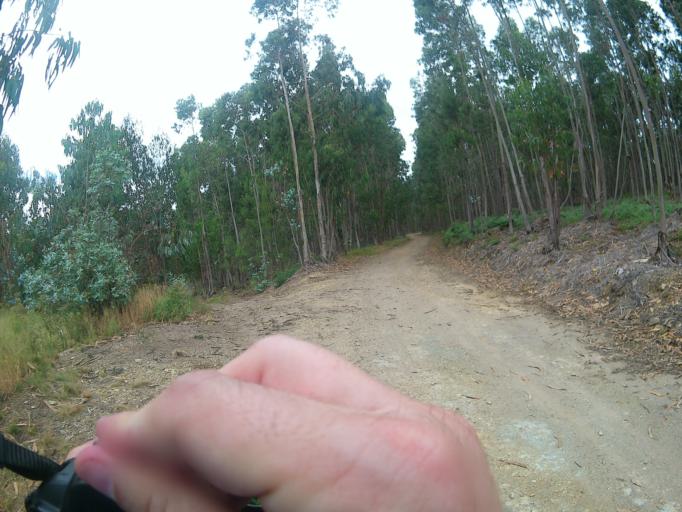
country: PT
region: Aveiro
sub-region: Albergaria-A-Velha
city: Branca
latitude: 40.7619
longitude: -8.4320
